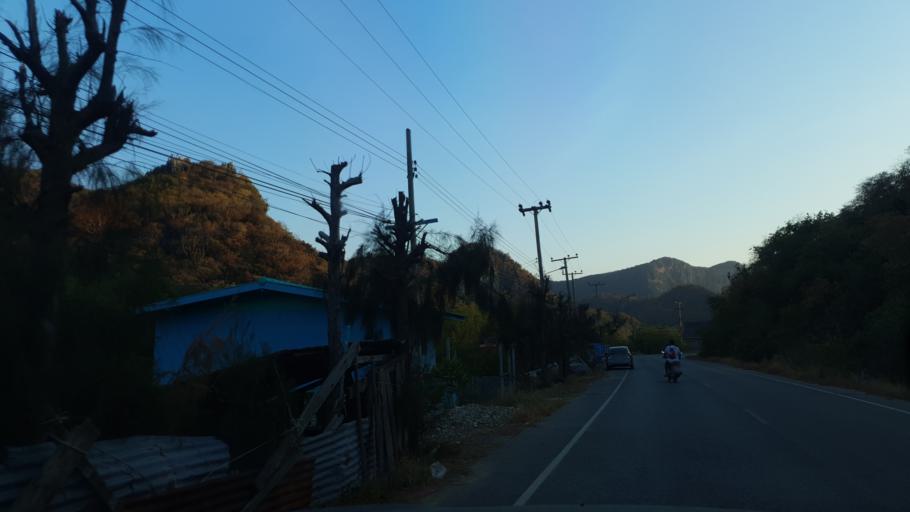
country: TH
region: Prachuap Khiri Khan
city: Sam Roi Yot
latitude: 12.2001
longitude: 100.0059
